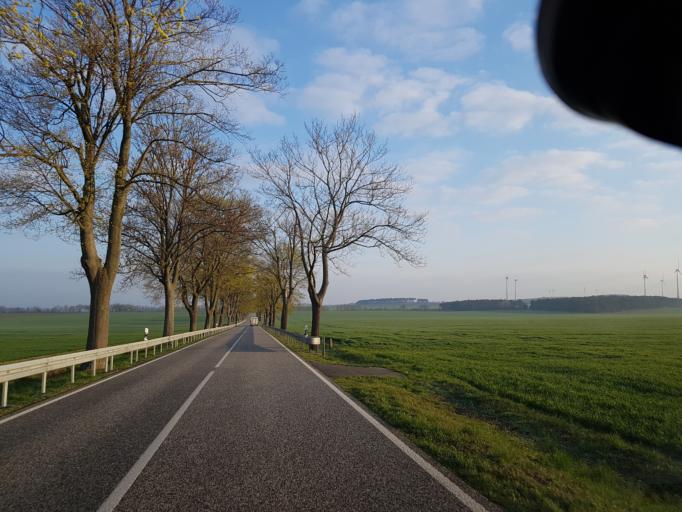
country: DE
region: Brandenburg
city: Juterbog
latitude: 51.9471
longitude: 13.1169
